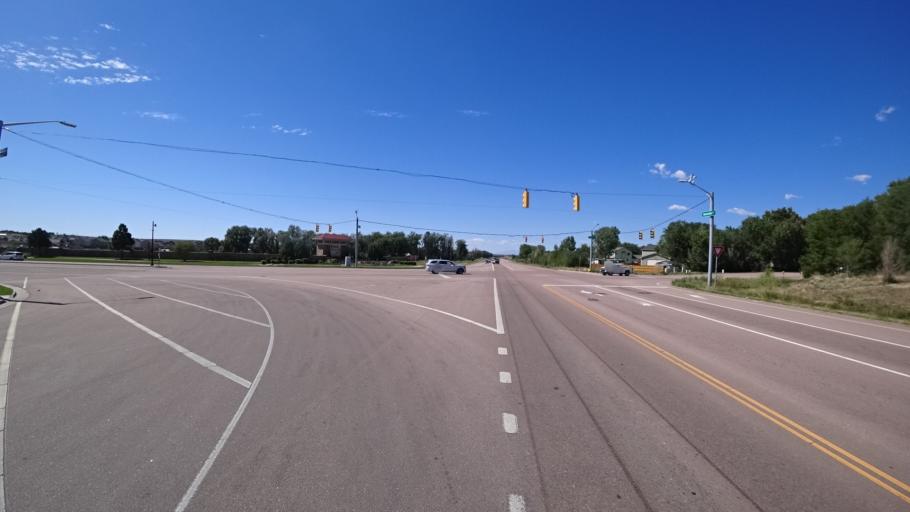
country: US
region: Colorado
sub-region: El Paso County
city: Security-Widefield
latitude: 38.7379
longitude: -104.6496
